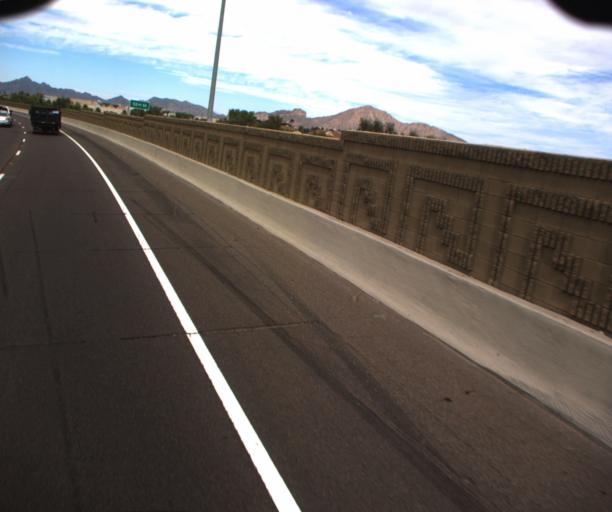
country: US
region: Arizona
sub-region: Maricopa County
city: Tempe Junction
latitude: 33.4523
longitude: -111.9691
